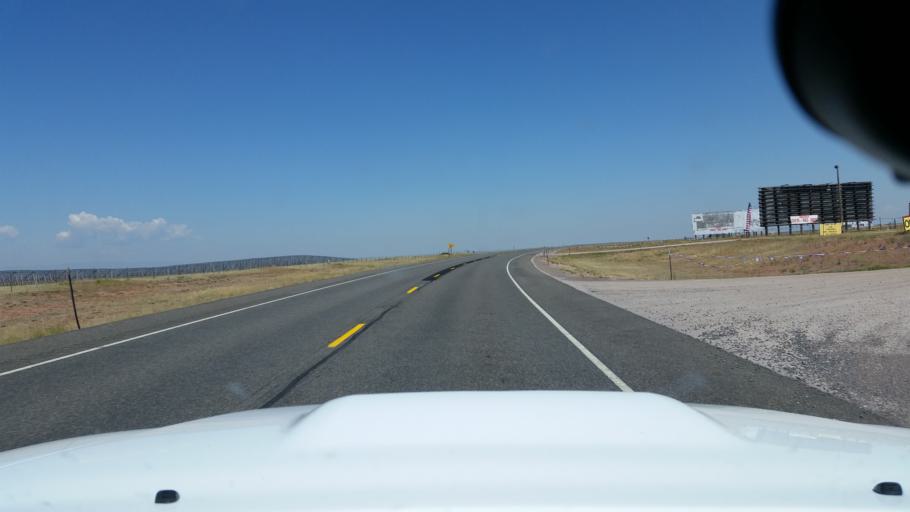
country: US
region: Wyoming
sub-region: Albany County
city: Laramie
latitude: 41.1265
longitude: -105.5500
